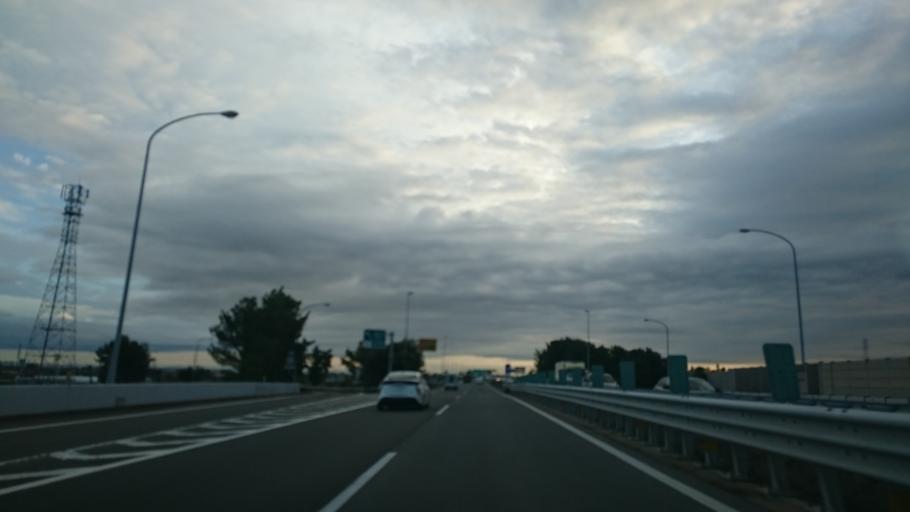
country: JP
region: Aichi
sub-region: Tsushima-shi
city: Tsushima
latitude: 35.1098
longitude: 136.6928
